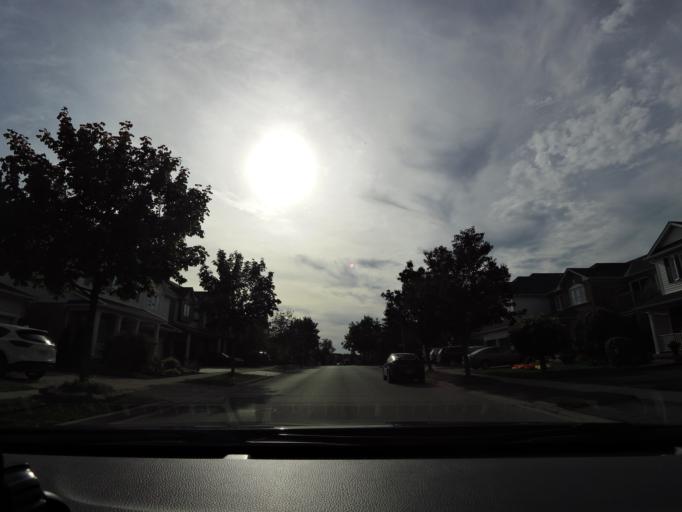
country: CA
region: Ontario
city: Burlington
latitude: 43.4001
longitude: -79.7901
